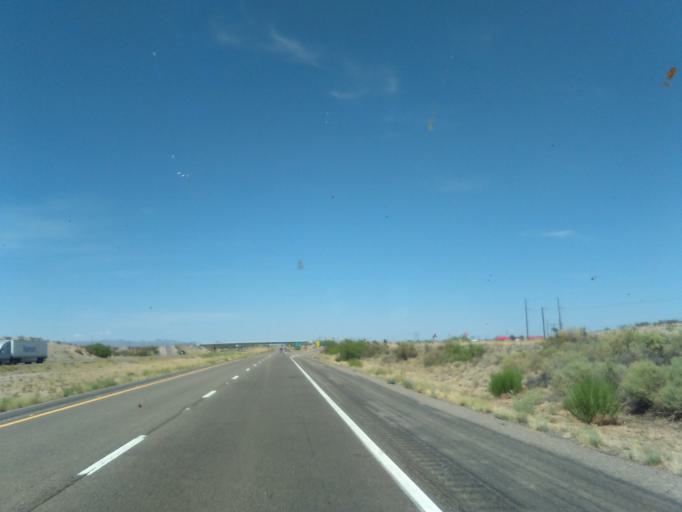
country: US
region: New Mexico
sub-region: Socorro County
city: Socorro
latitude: 33.6331
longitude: -107.1249
